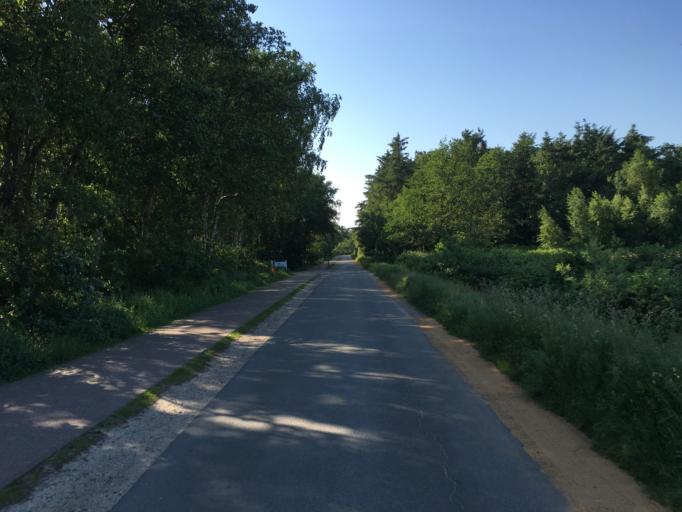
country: DE
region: Schleswig-Holstein
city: Norddorf
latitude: 54.6826
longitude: 8.3291
